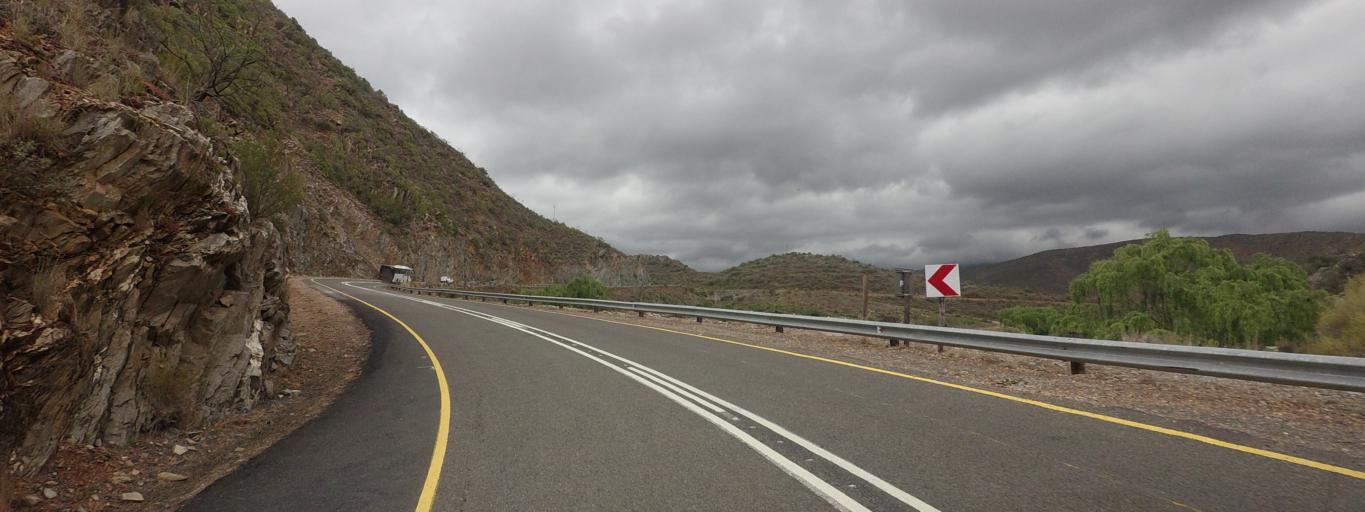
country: ZA
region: Western Cape
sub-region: Eden District Municipality
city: Oudtshoorn
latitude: -33.4189
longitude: 22.2409
